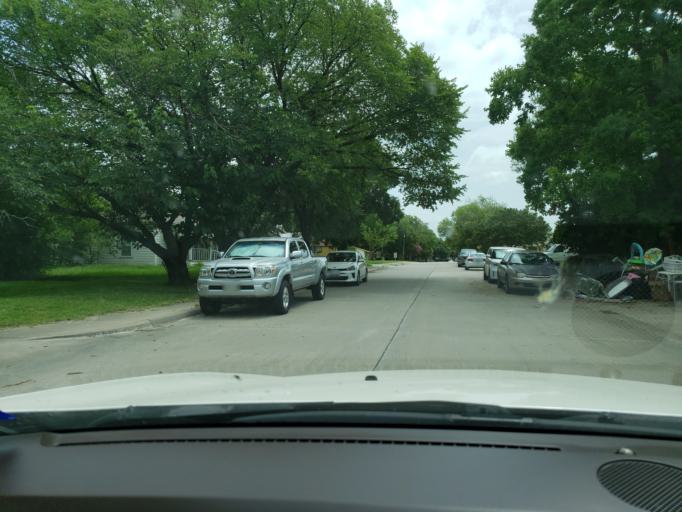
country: US
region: Texas
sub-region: Dallas County
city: Rowlett
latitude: 32.9008
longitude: -96.5689
